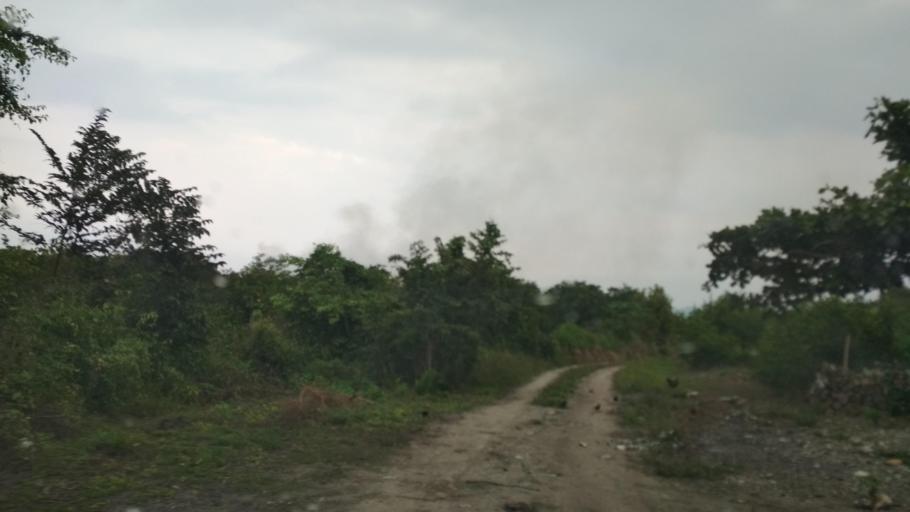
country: MM
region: Shan
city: Taunggyi
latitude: 20.3199
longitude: 97.3029
